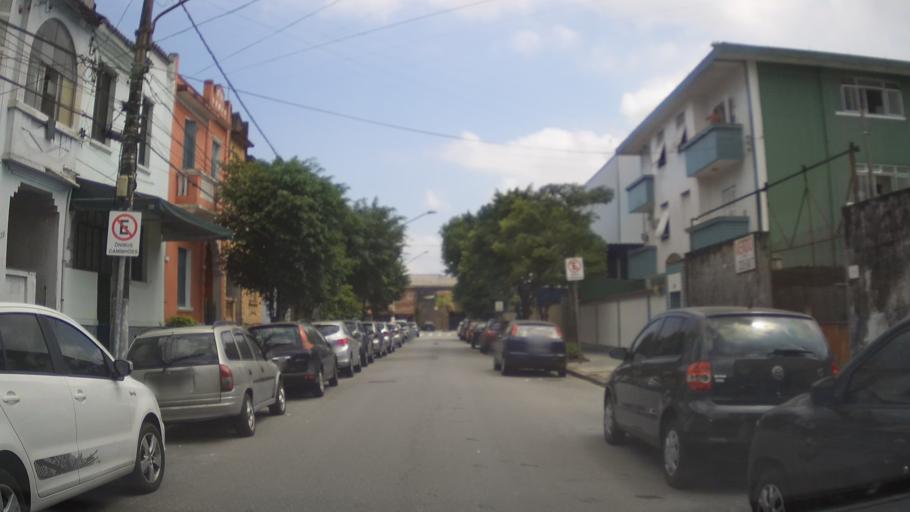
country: BR
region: Sao Paulo
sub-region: Santos
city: Santos
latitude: -23.9481
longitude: -46.3209
